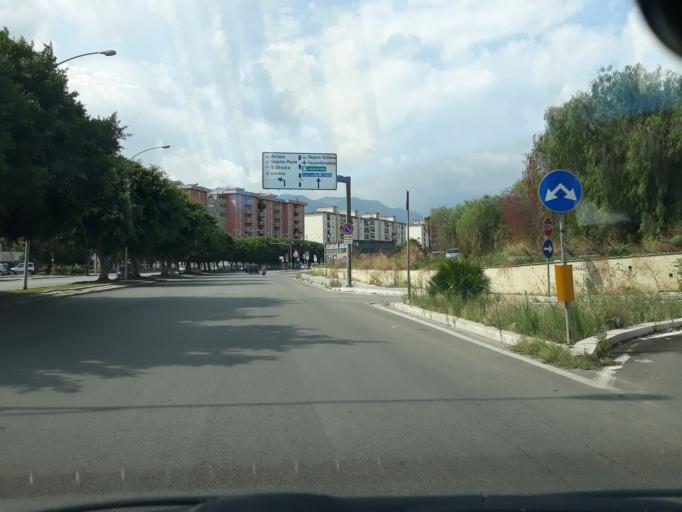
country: IT
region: Sicily
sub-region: Palermo
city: Palermo
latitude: 38.0993
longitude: 13.3466
